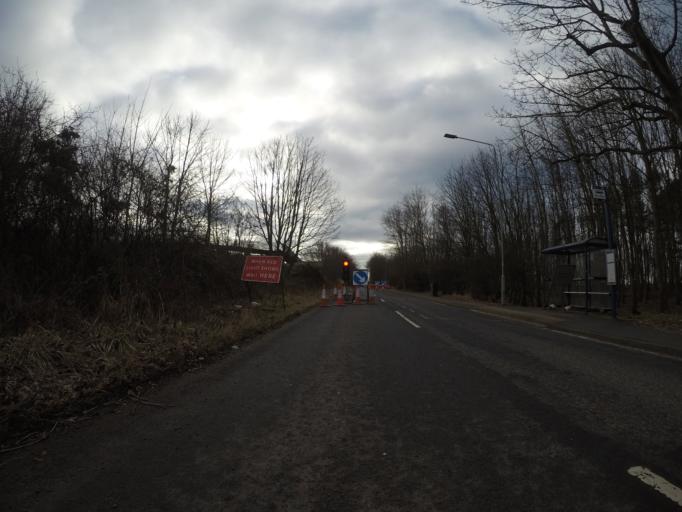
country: GB
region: Scotland
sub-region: North Ayrshire
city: Dreghorn
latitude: 55.5855
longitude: -4.6472
